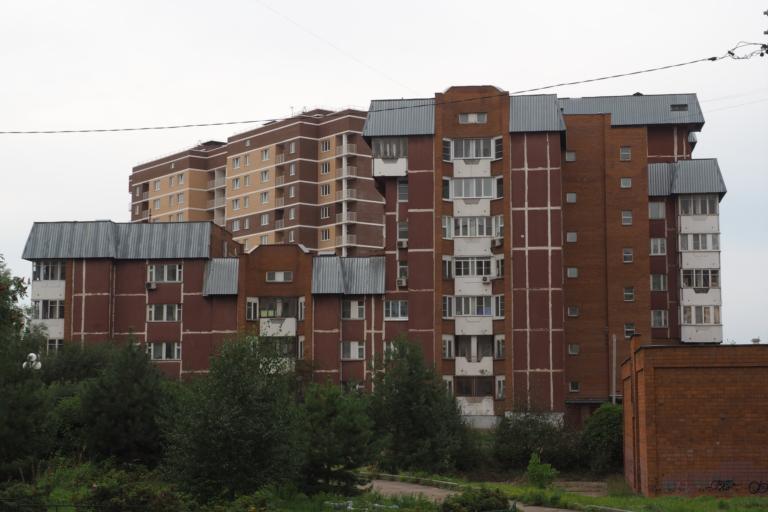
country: RU
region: Moskovskaya
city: Pushchino
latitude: 54.8320
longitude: 37.6369
